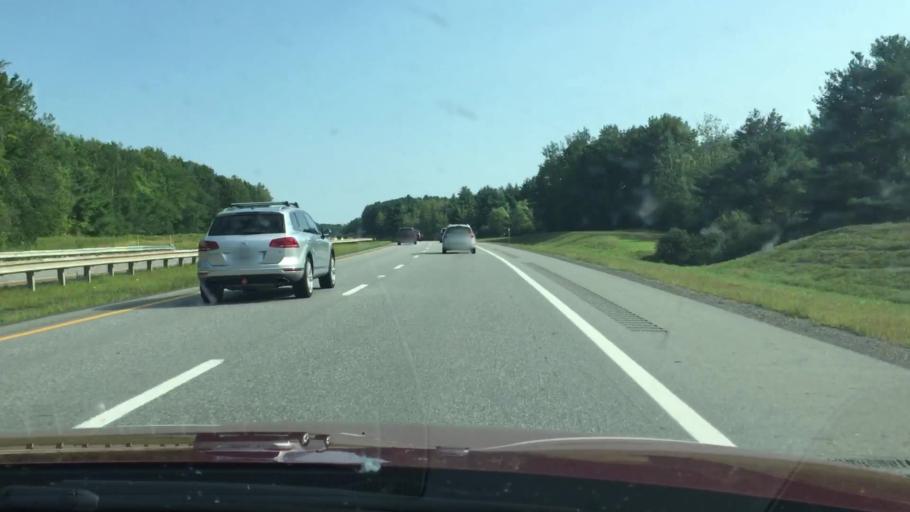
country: US
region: Maine
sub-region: Cumberland County
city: Cumberland Center
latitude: 43.7642
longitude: -70.3115
